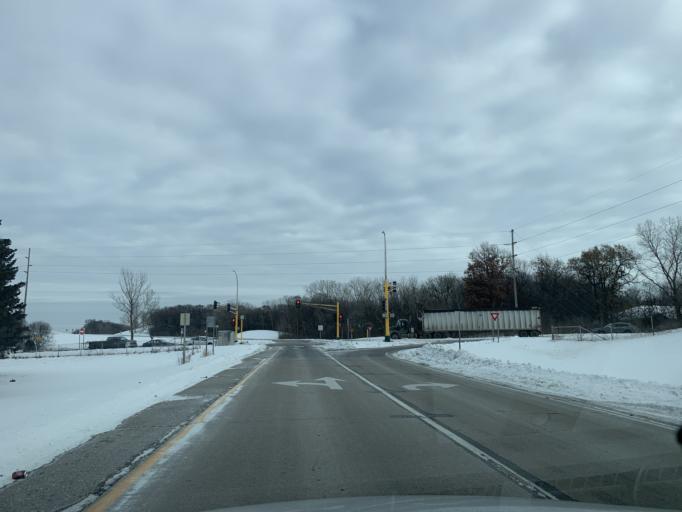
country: US
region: Minnesota
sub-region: Dakota County
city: Burnsville
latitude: 44.7582
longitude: -93.2490
